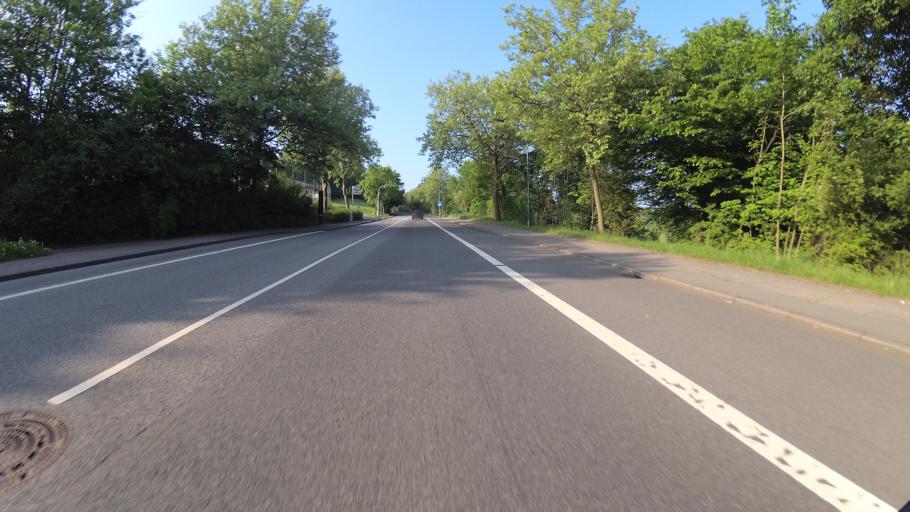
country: DE
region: Saarland
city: Neunkirchen
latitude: 49.3435
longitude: 7.1908
